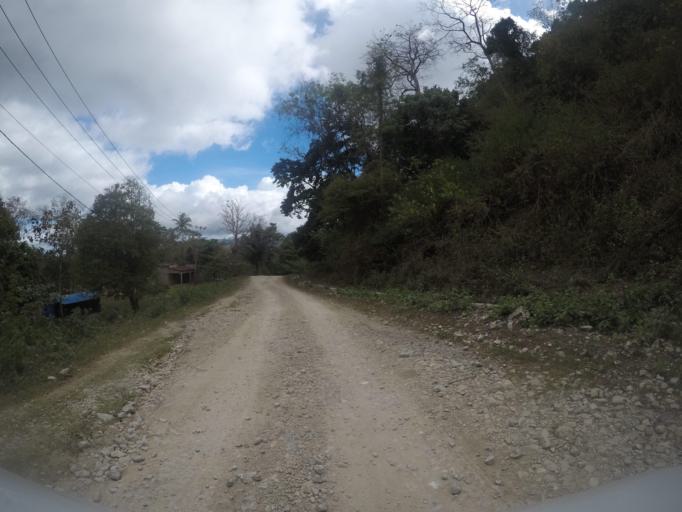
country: TL
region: Lautem
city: Lospalos
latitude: -8.5512
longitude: 126.8992
